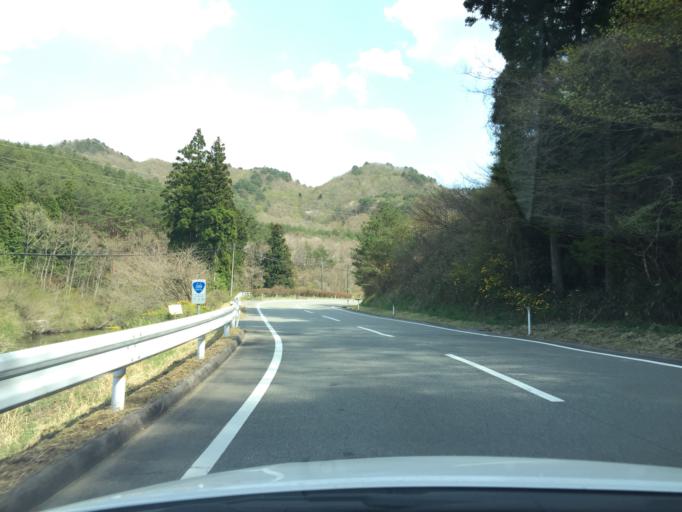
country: JP
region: Fukushima
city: Namie
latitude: 37.2955
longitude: 140.8371
